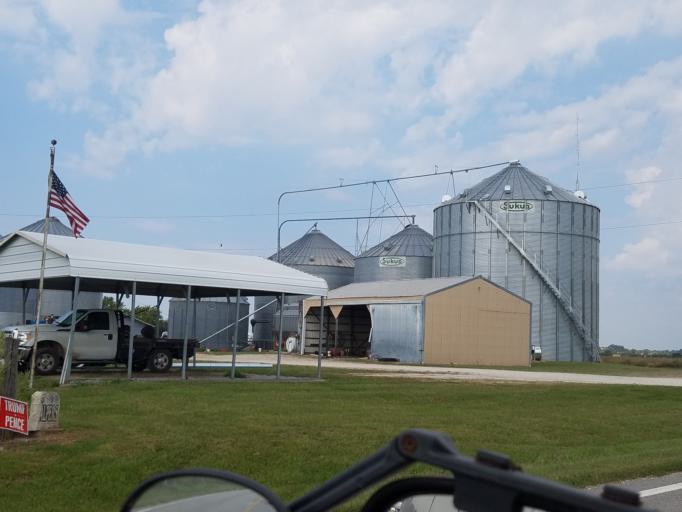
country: US
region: Missouri
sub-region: Cooper County
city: Boonville
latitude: 38.8647
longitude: -92.6409
